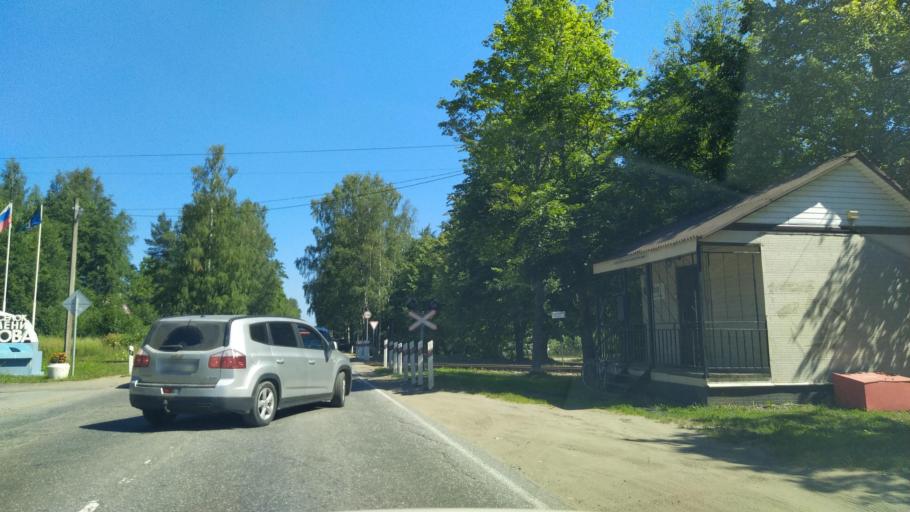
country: RU
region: Leningrad
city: Imeni Morozova
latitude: 59.9706
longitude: 31.0232
